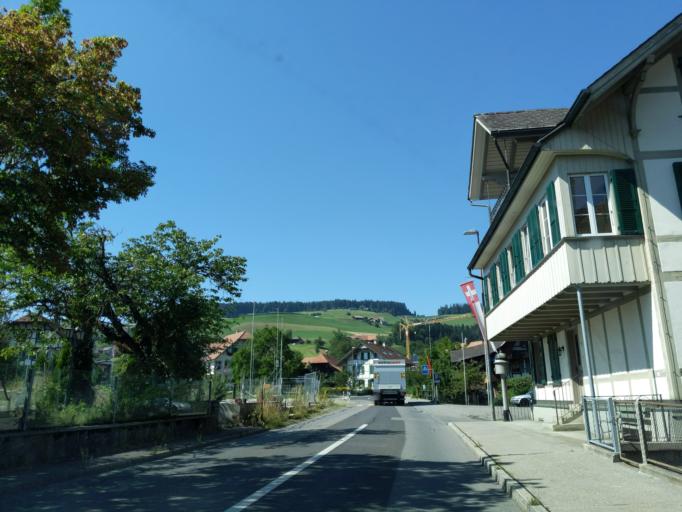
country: CH
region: Bern
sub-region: Bern-Mittelland District
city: Zaziwil
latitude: 46.9000
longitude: 7.6605
